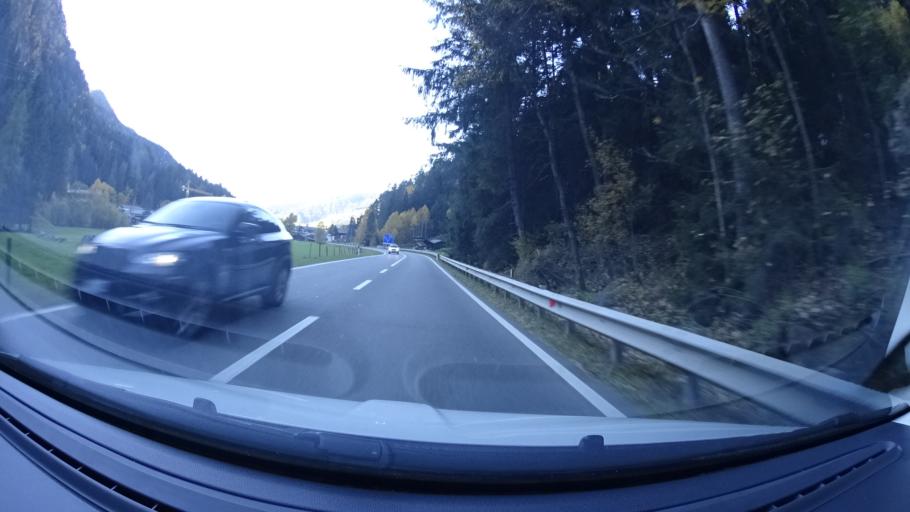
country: IT
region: Trentino-Alto Adige
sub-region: Bolzano
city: Ortisei
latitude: 46.5824
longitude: 11.6381
